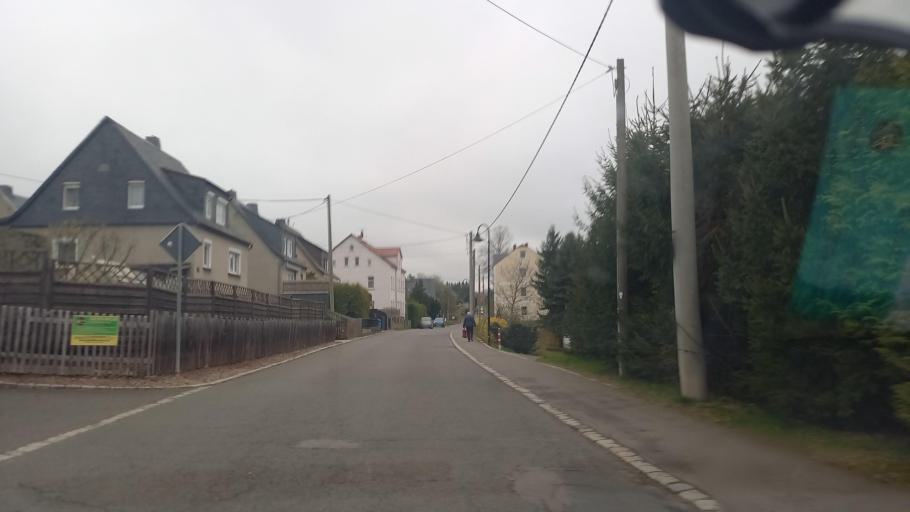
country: DE
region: Saxony
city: Reinsdorf
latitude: 50.6971
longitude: 12.5662
